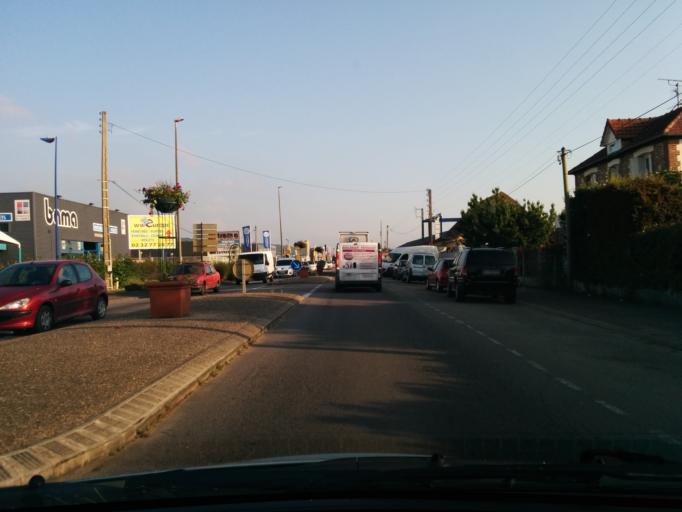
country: FR
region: Haute-Normandie
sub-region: Departement de l'Eure
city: Saint-Marcel
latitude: 49.1080
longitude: 1.4553
